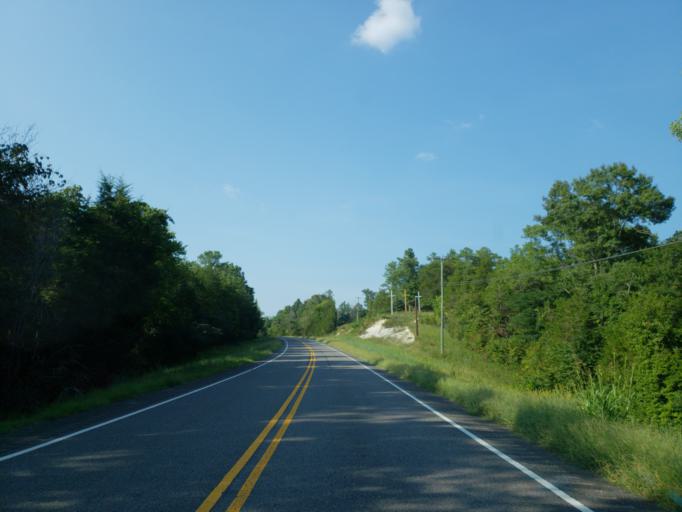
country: US
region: Alabama
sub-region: Sumter County
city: Livingston
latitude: 32.6406
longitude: -88.1719
